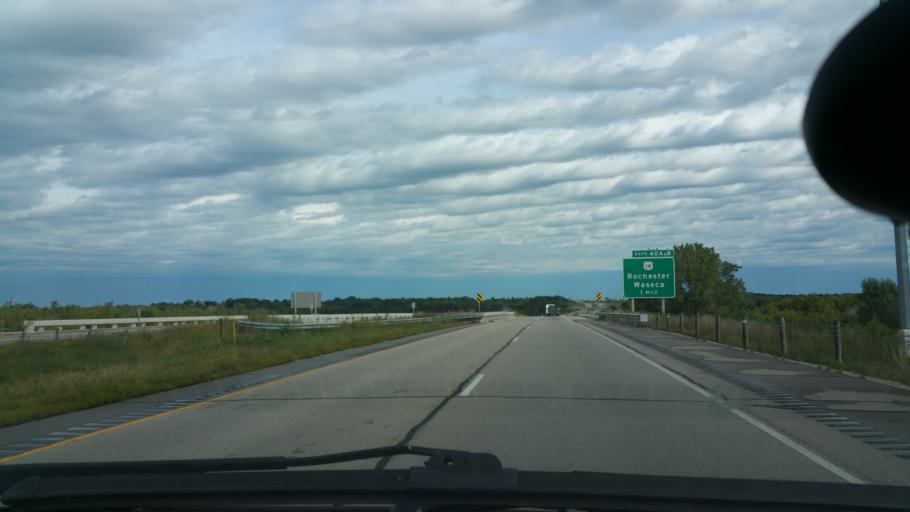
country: US
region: Minnesota
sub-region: Steele County
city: Owatonna
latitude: 44.0406
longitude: -93.2485
